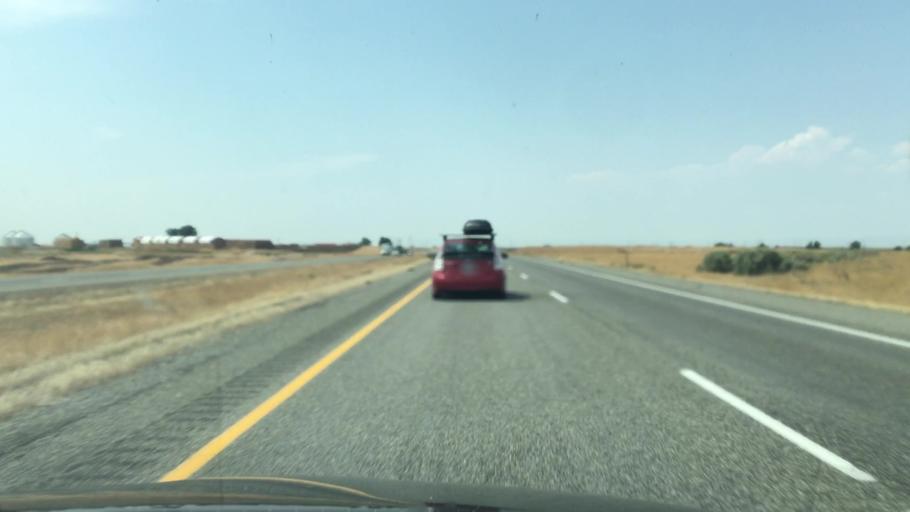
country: US
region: Idaho
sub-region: Gooding County
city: Wendell
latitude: 42.8040
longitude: -114.7645
